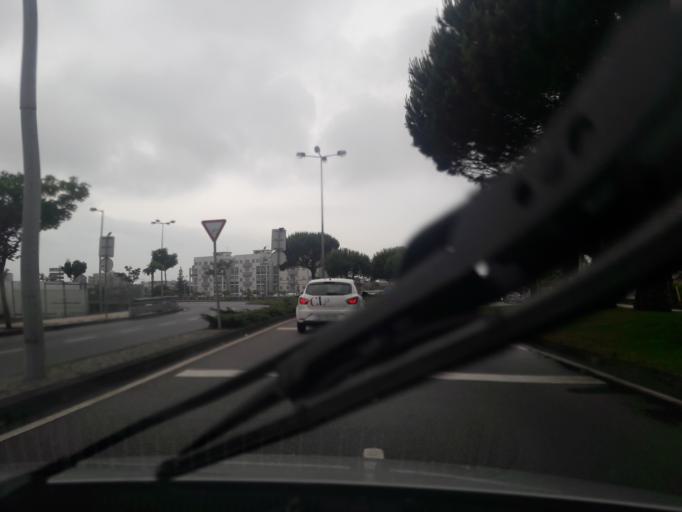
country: PT
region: Porto
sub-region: Povoa de Varzim
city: Povoa de Varzim
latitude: 41.3902
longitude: -8.7613
